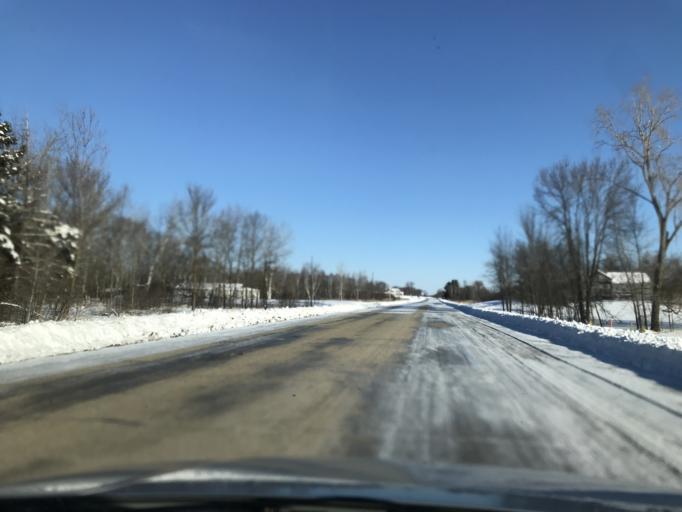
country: US
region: Wisconsin
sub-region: Oconto County
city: Oconto Falls
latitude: 44.9613
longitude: -88.0464
